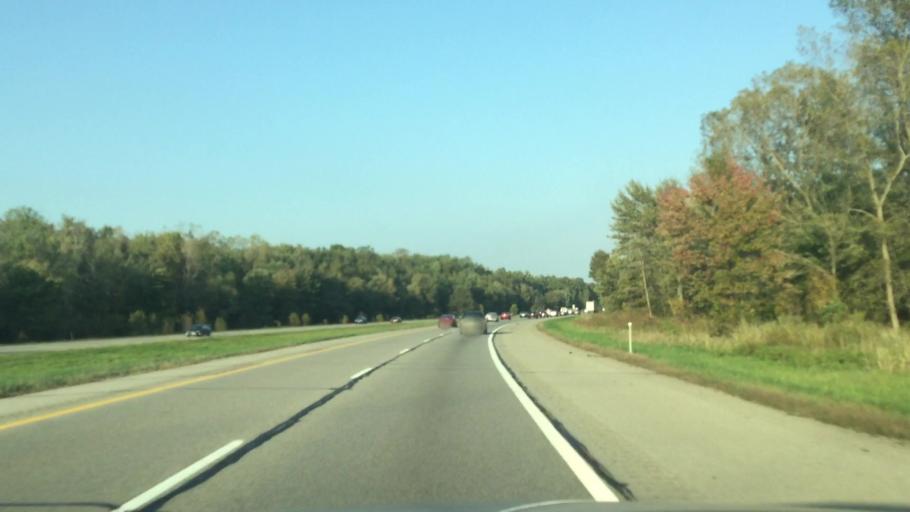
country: US
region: Michigan
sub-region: Wayne County
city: Canton
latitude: 42.3556
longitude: -83.5873
